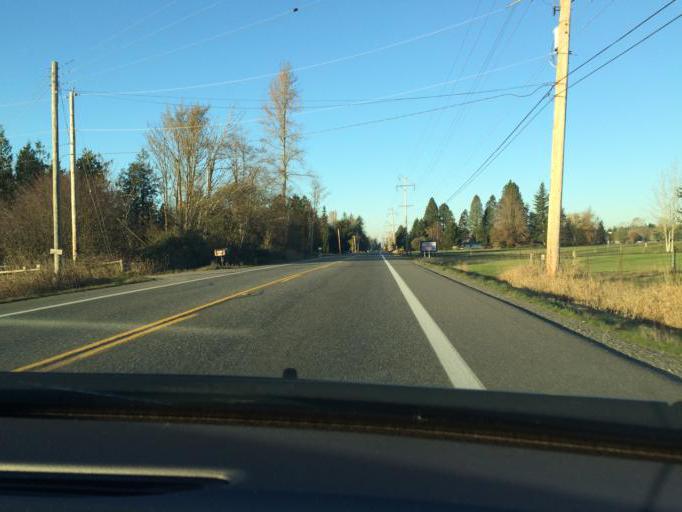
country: US
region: Washington
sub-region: Whatcom County
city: Bellingham
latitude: 48.8107
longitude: -122.4430
